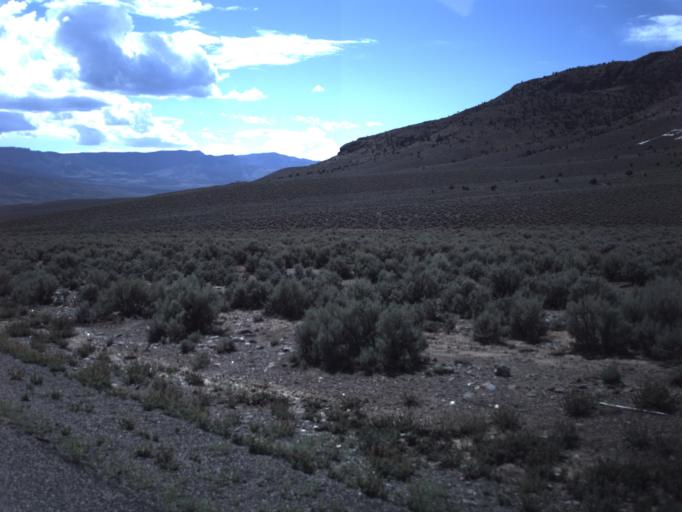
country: US
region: Utah
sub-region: Piute County
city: Junction
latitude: 38.2522
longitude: -112.2407
